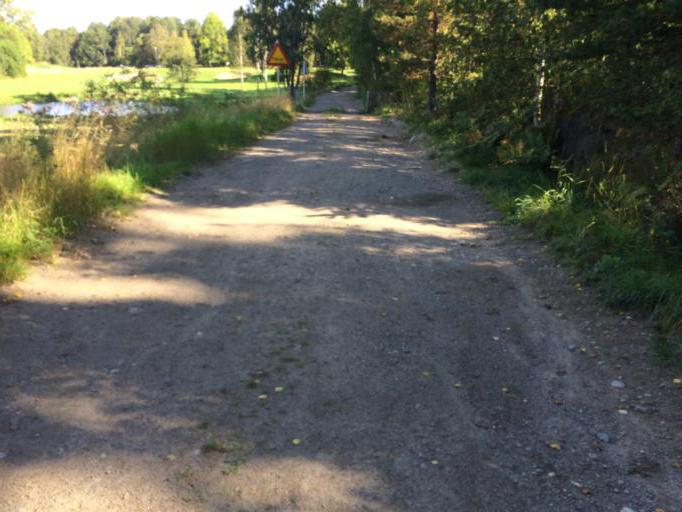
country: SE
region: Stockholm
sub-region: Haninge Kommun
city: Handen
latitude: 59.2206
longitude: 18.0993
